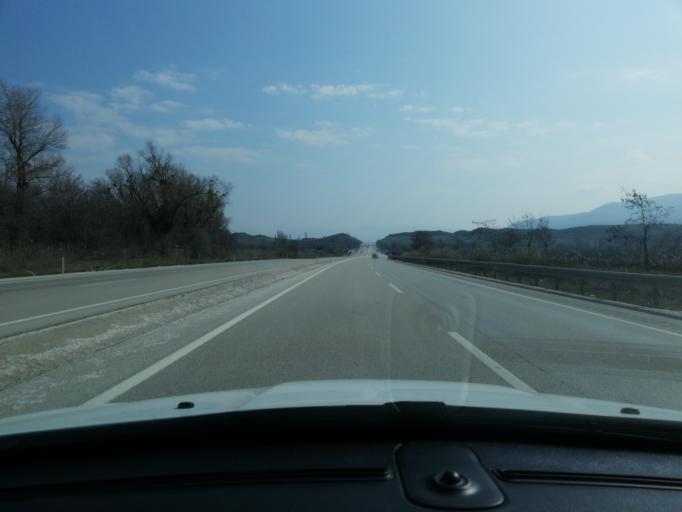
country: TR
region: Cankiri
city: Beloren
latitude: 40.8744
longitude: 33.5020
